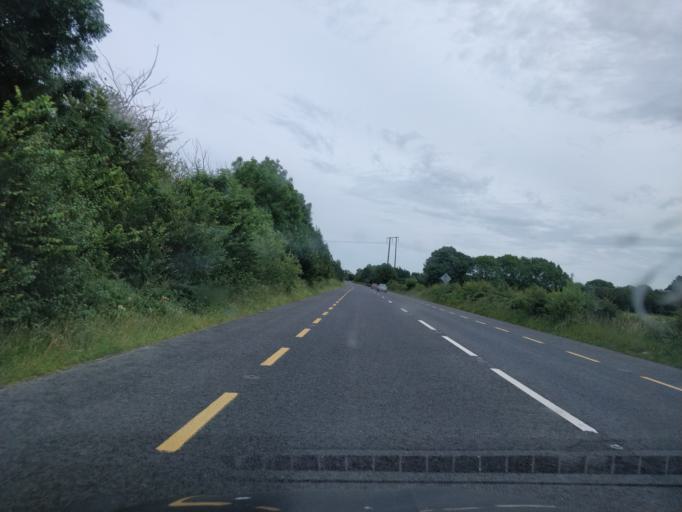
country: IE
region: Leinster
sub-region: Uibh Fhaili
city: Ferbane
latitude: 53.1675
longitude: -7.7692
